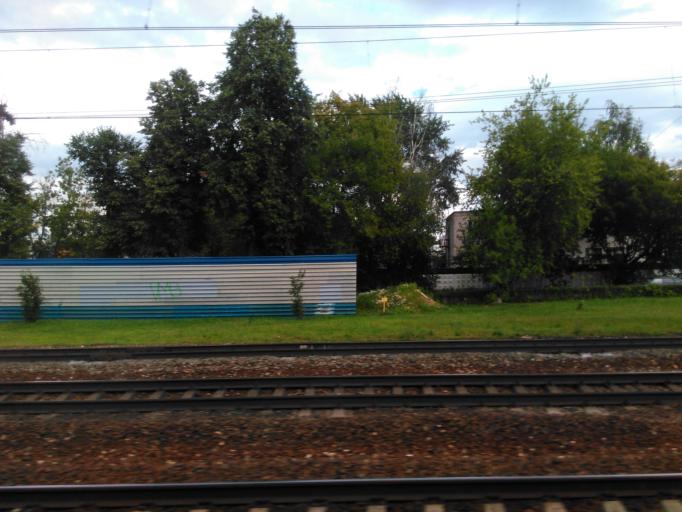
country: RU
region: Moscow
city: Rostokino
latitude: 55.8397
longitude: 37.6699
